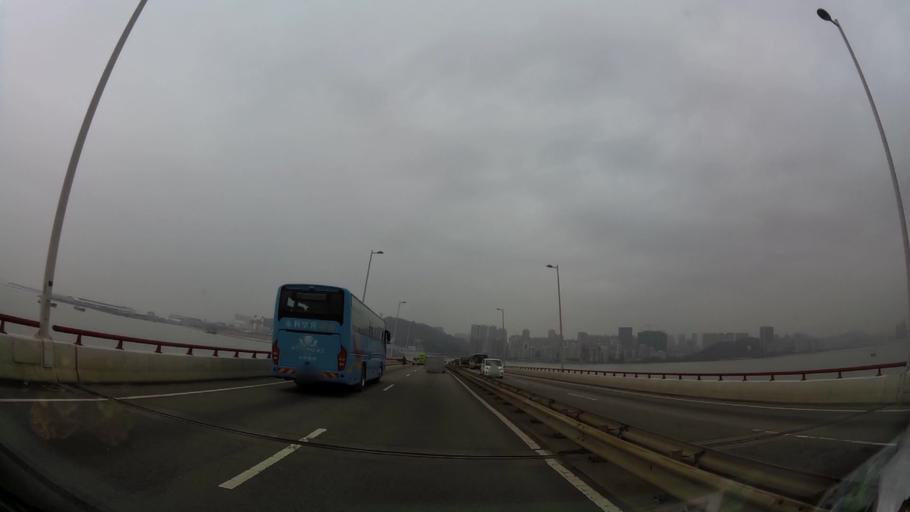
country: MO
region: Macau
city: Macau
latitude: 22.1792
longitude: 113.5634
